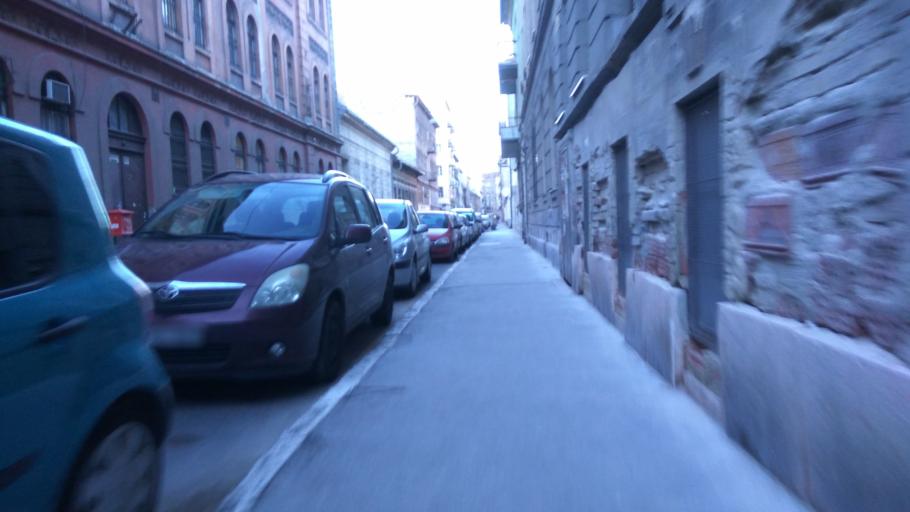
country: HU
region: Budapest
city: Budapest VIII. keruelet
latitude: 47.4920
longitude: 19.0757
